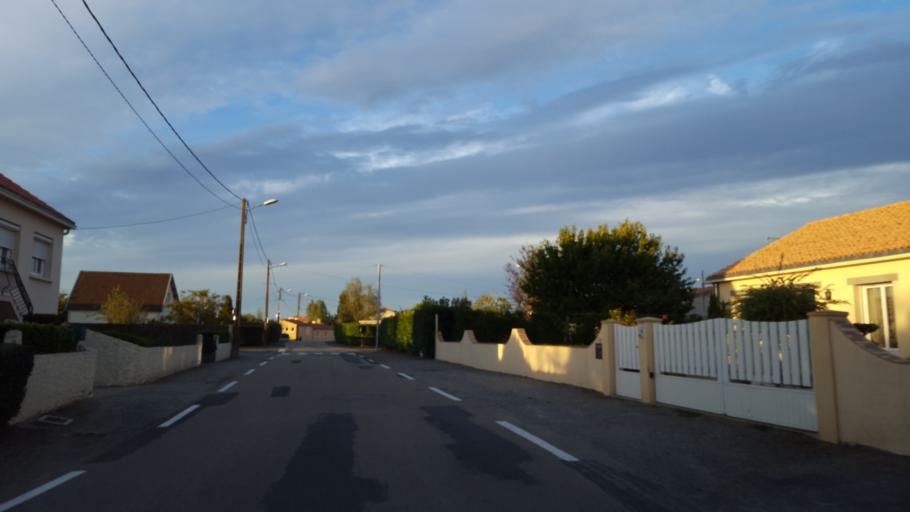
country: FR
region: Pays de la Loire
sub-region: Departement de la Loire-Atlantique
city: Basse-Goulaine
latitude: 47.2084
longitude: -1.4726
